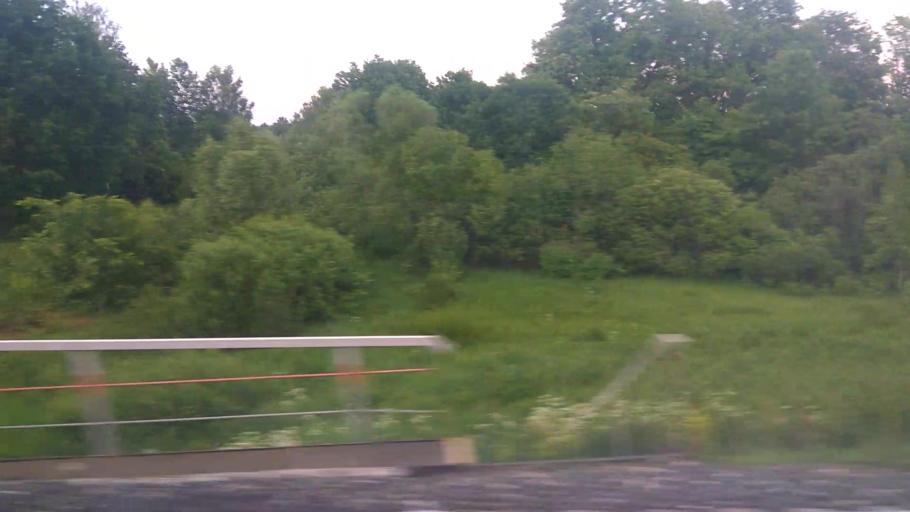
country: RU
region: Moskovskaya
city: Zhilevo
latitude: 55.0698
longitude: 37.9831
